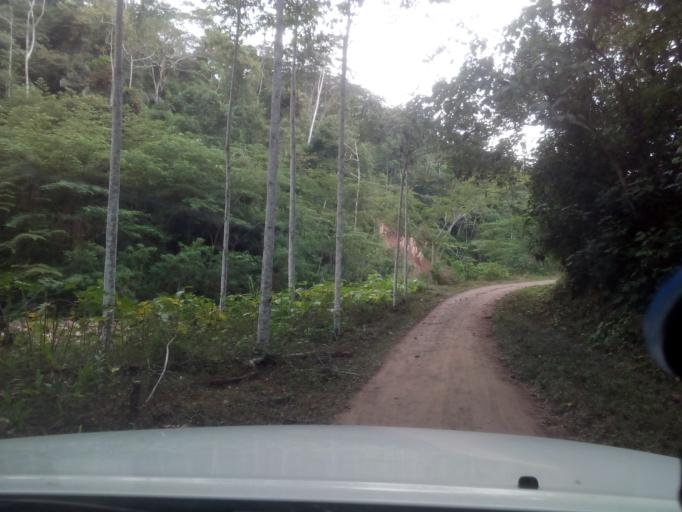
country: PE
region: Pasco
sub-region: Provincia de Oxapampa
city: Villa Rica
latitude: -10.8114
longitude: -75.2608
